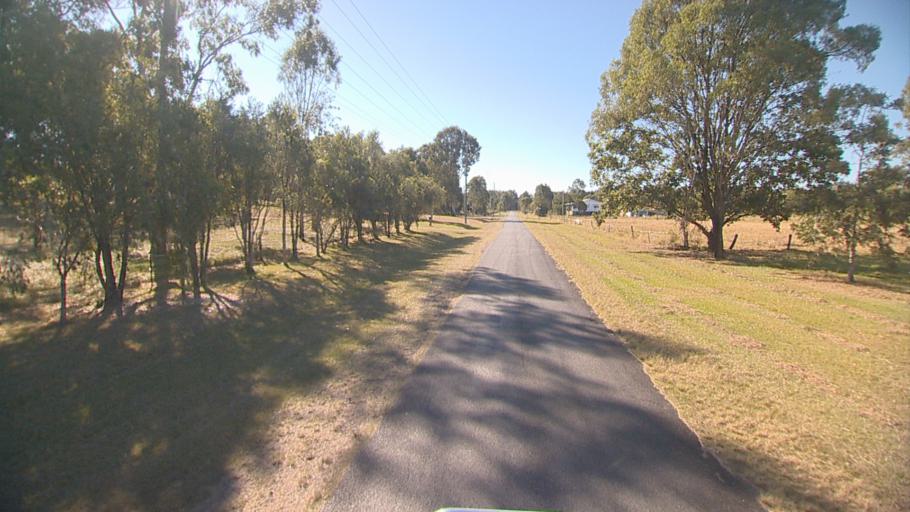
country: AU
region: Queensland
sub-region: Logan
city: North Maclean
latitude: -27.7812
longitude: 153.0189
